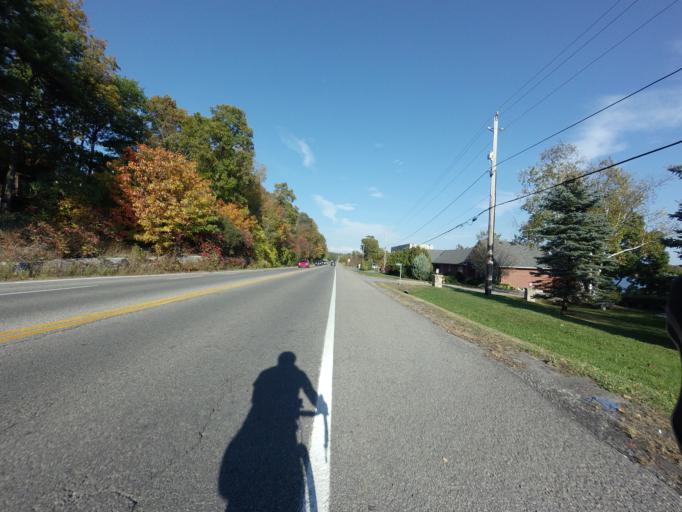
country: CA
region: Ontario
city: Kingston
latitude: 44.2364
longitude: -76.6200
